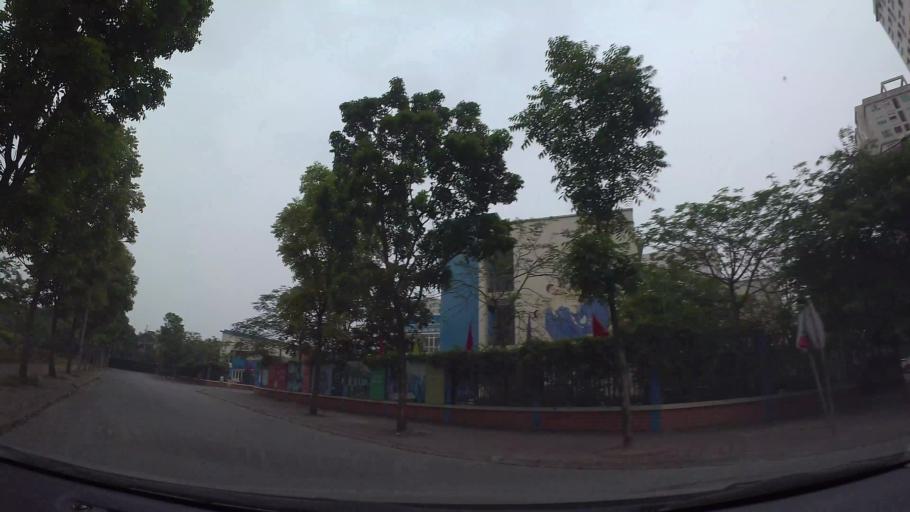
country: VN
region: Ha Noi
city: Trau Quy
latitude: 21.0392
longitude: 105.9105
